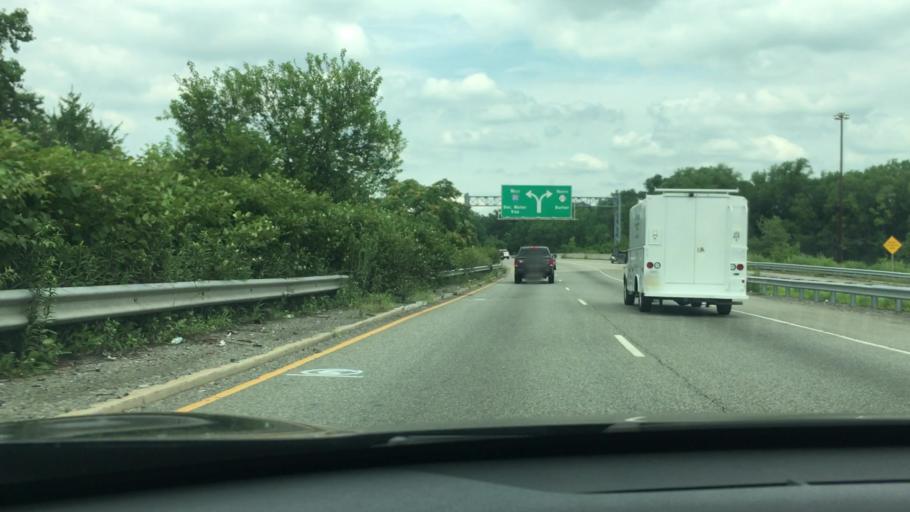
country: US
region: New Jersey
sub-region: Passaic County
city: Singac
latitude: 40.8961
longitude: -74.2488
